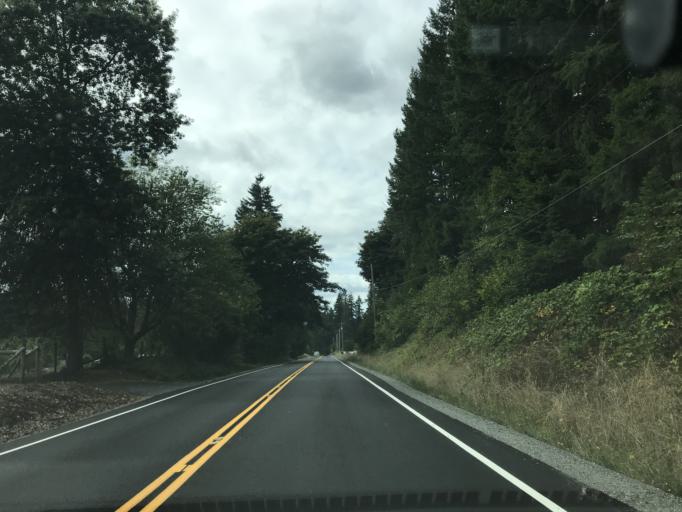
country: US
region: Washington
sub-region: King County
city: Black Diamond
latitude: 47.2868
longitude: -122.0152
